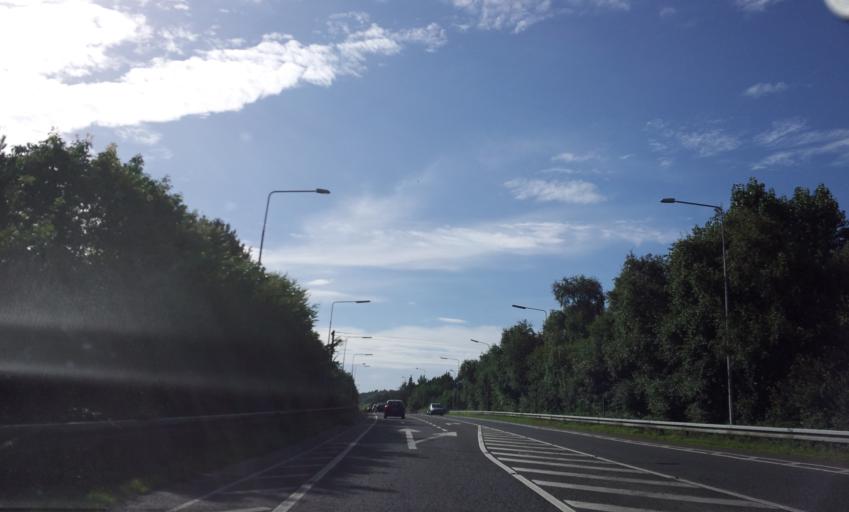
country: IE
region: Munster
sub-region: Ciarrai
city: Cill Airne
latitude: 52.0691
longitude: -9.5028
